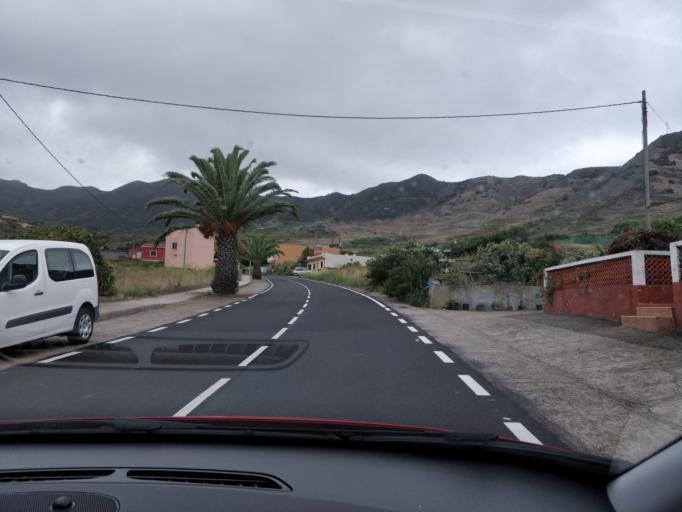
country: ES
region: Canary Islands
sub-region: Provincia de Santa Cruz de Tenerife
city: Tanque
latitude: 28.3363
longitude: -16.8518
